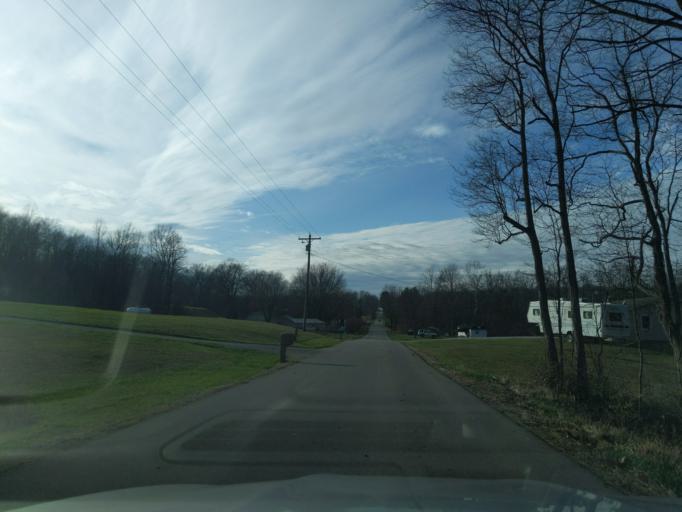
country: US
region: Indiana
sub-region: Decatur County
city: Westport
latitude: 39.1903
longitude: -85.5091
